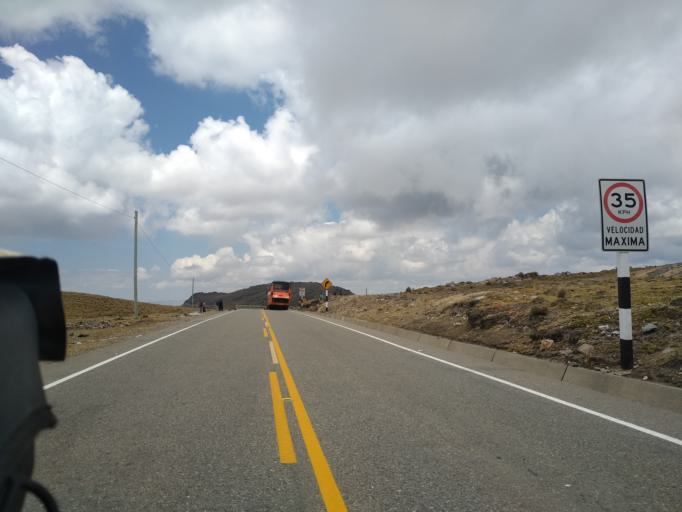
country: PE
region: La Libertad
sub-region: Provincia de Santiago de Chuco
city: Quiruvilca
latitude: -7.9680
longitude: -78.1993
